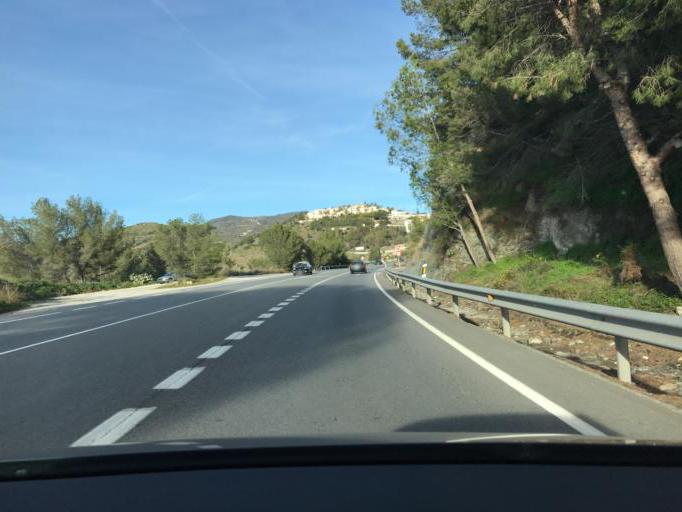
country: ES
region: Andalusia
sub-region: Provincia de Granada
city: Almunecar
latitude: 36.7412
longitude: -3.6758
